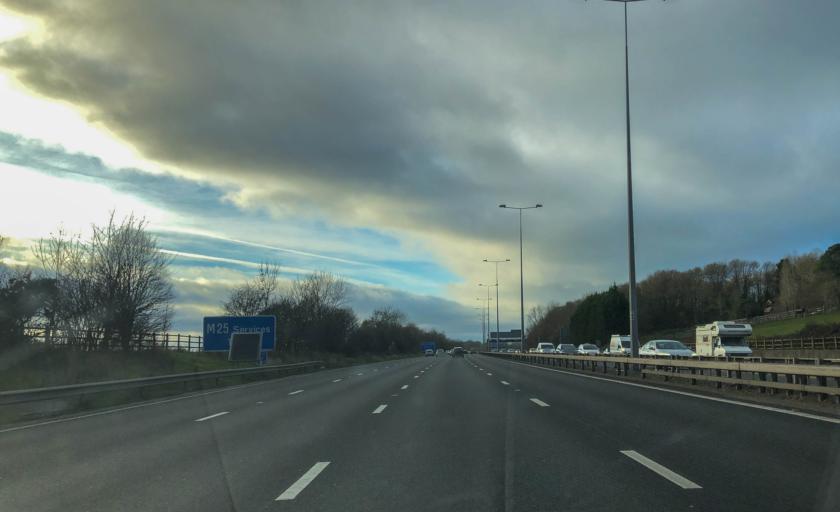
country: GB
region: England
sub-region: Surrey
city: Godstone
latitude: 51.2578
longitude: -0.0794
